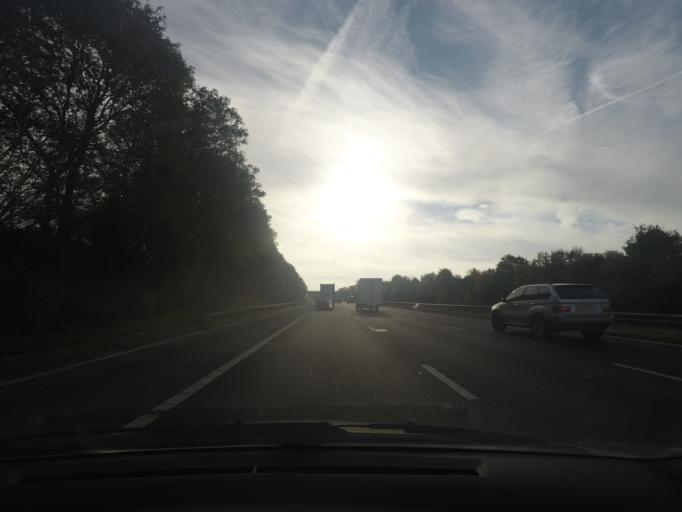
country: GB
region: England
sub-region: Barnsley
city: Dodworth
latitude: 53.5574
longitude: -1.5309
